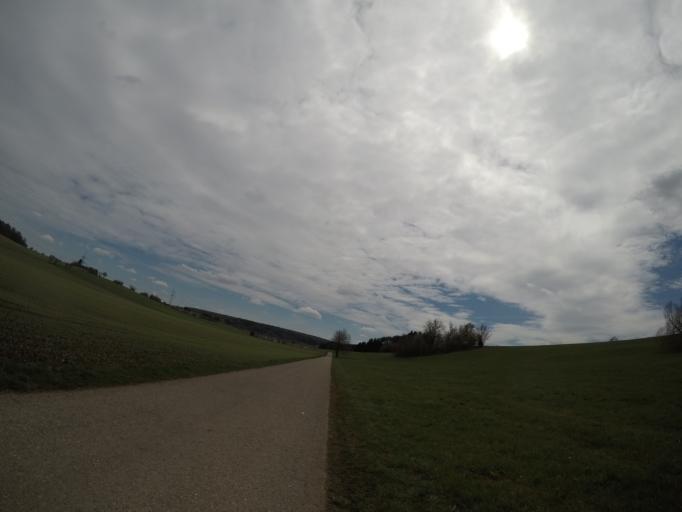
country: DE
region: Baden-Wuerttemberg
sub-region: Tuebingen Region
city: Westerheim
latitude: 48.5052
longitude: 9.6455
